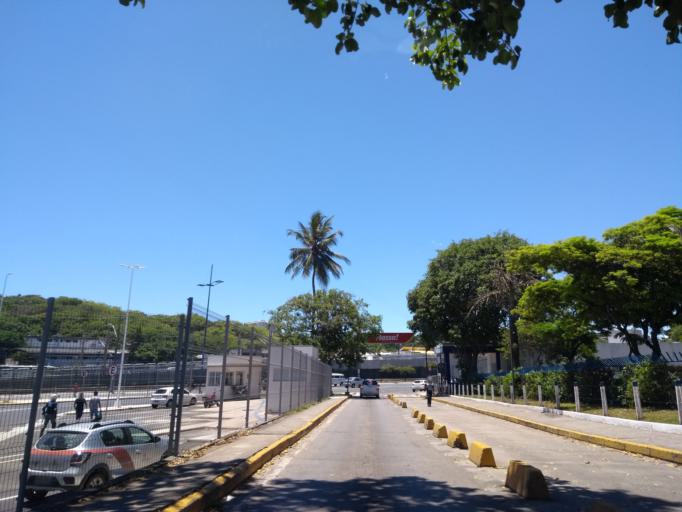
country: BR
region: Bahia
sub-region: Salvador
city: Salvador
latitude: -12.9787
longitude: -38.4666
